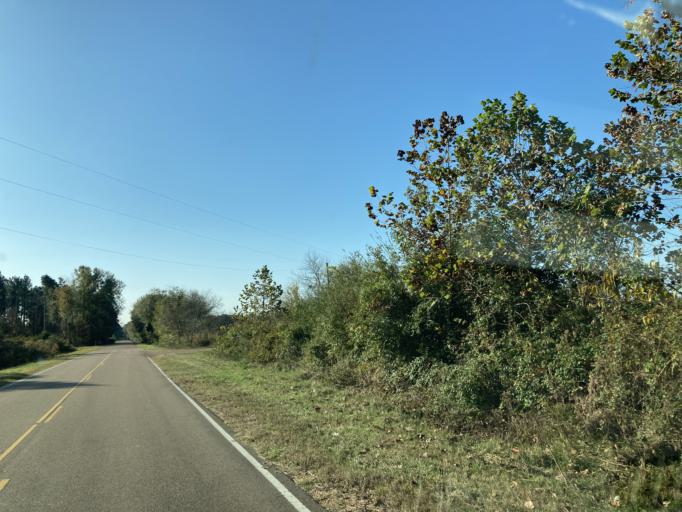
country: US
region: Mississippi
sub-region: Madison County
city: Canton
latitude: 32.7280
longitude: -90.1667
